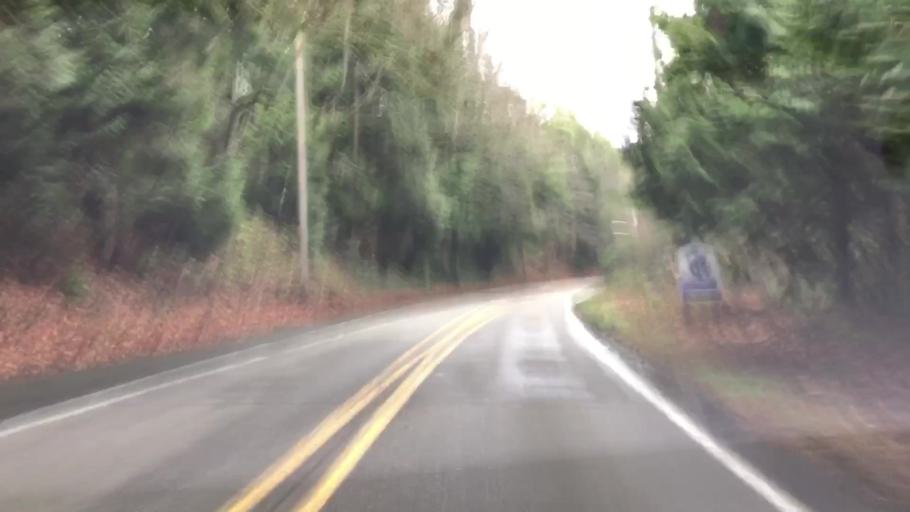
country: US
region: Washington
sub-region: King County
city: Sammamish
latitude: 47.6184
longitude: -122.0985
